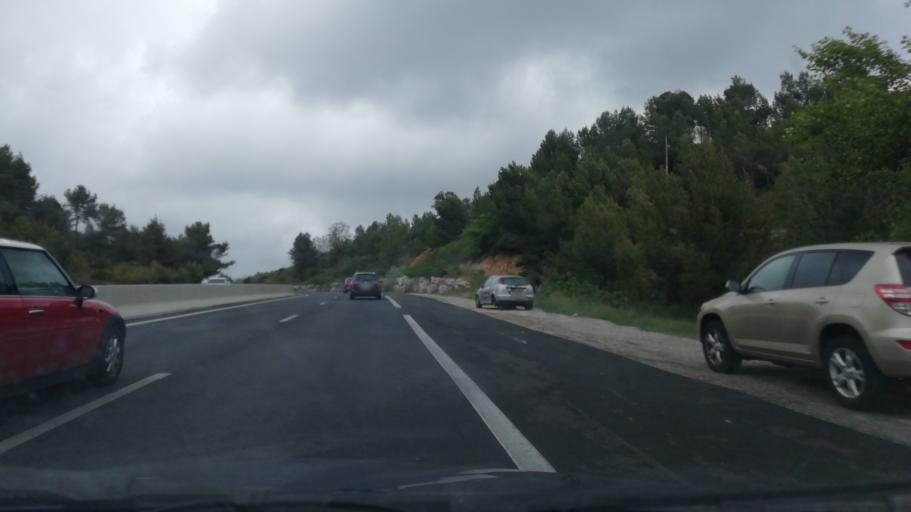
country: FR
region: Languedoc-Roussillon
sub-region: Departement de l'Herault
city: Saint-Clement-de-Riviere
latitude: 43.6619
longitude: 3.8307
